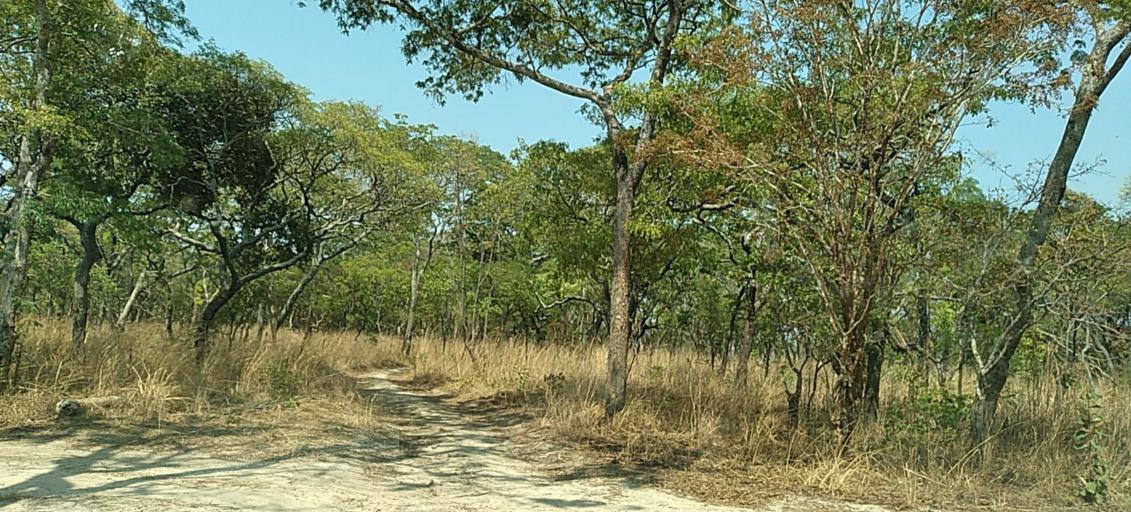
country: ZM
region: Copperbelt
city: Mpongwe
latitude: -13.7942
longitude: 28.0872
